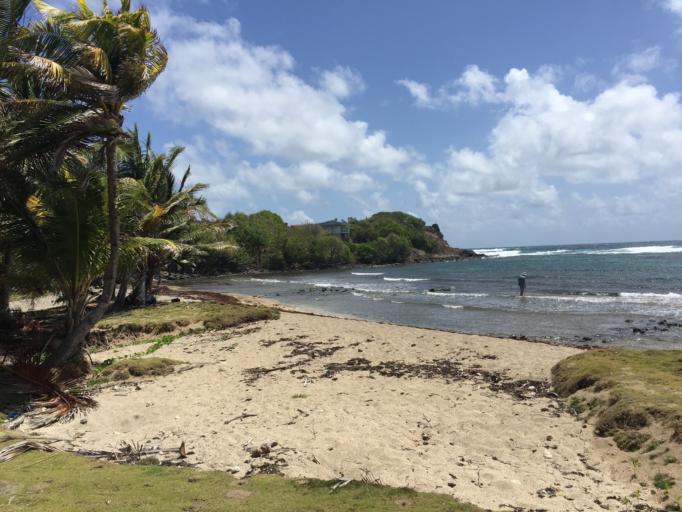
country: VC
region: Grenadines
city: Port Elizabeth
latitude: 13.0269
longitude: -61.2133
